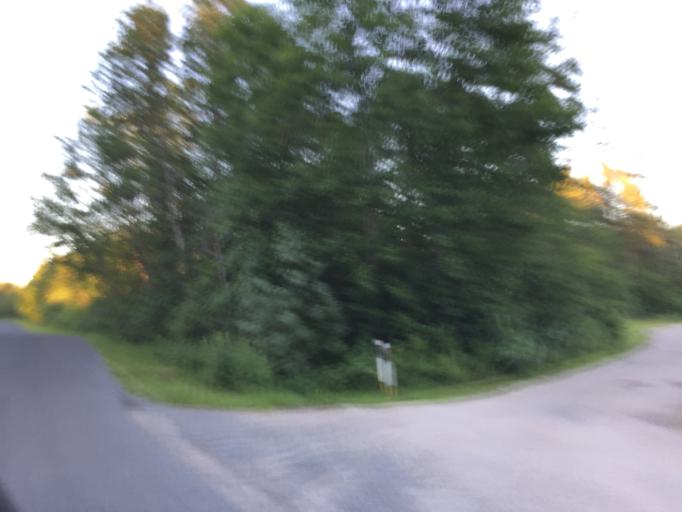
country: EE
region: Harju
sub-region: Raasiku vald
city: Raasiku
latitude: 59.4432
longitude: 25.1913
